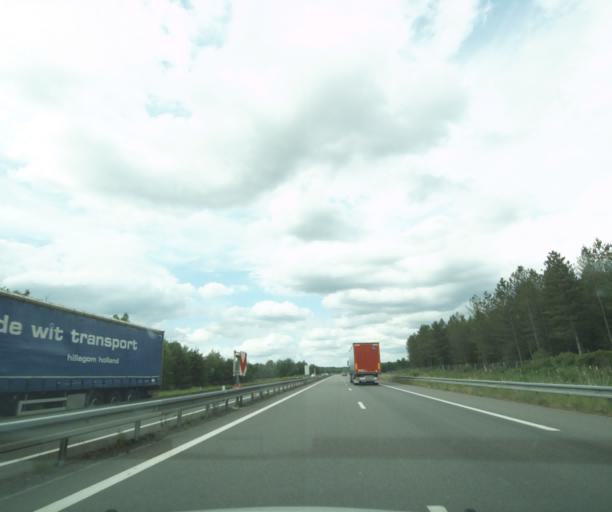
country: FR
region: Centre
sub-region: Departement du Loir-et-Cher
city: Theillay
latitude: 47.3274
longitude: 2.0487
